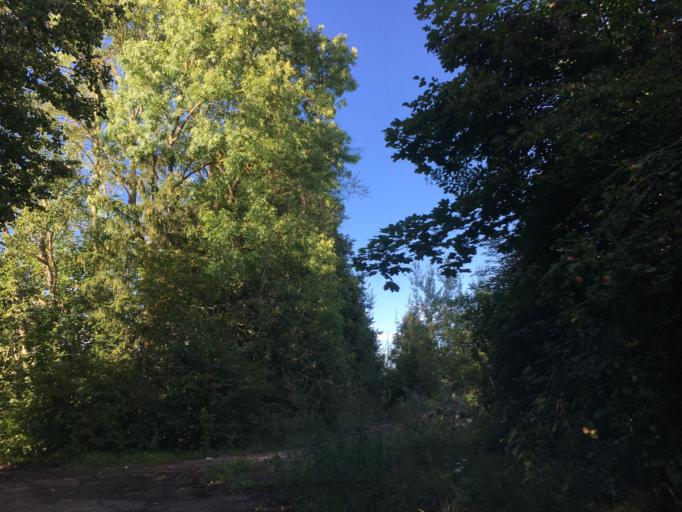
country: RU
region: Pskov
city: Izborsk
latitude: 57.7686
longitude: 27.9743
